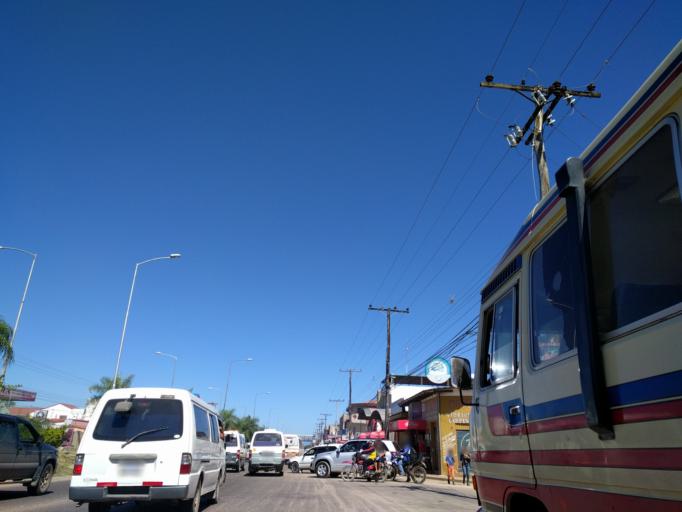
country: BO
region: Santa Cruz
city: Santa Cruz de la Sierra
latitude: -17.8263
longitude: -63.2247
